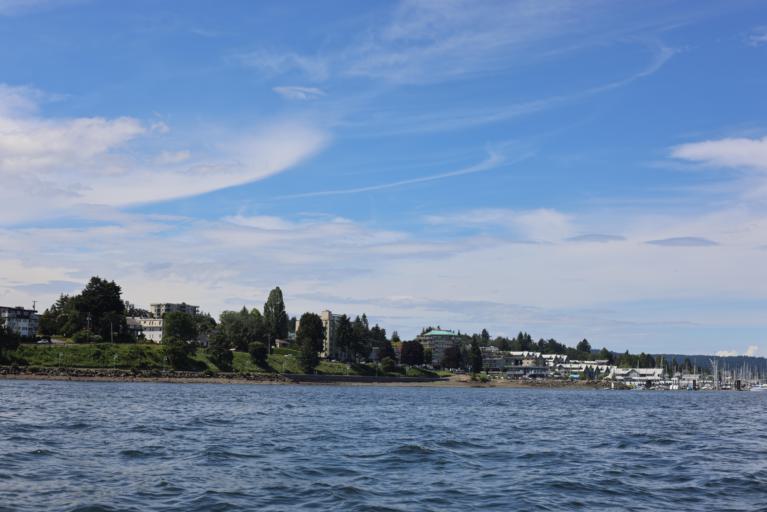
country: CA
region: British Columbia
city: Nanaimo
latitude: 49.1731
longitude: -123.9358
